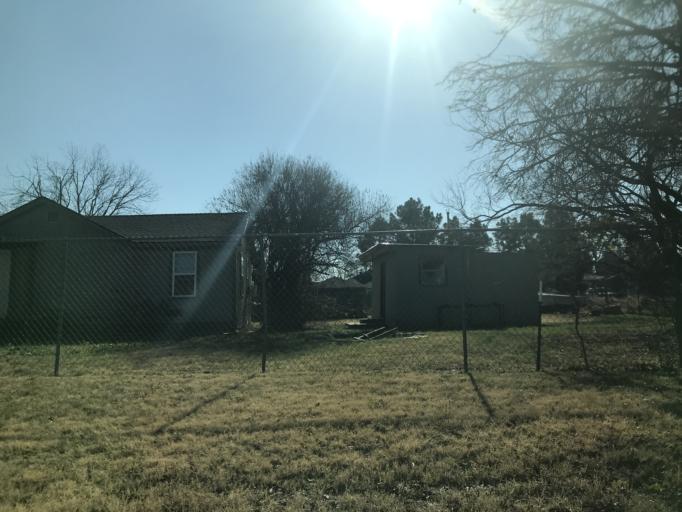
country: US
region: Texas
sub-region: Taylor County
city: Abilene
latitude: 32.4646
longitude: -99.7208
